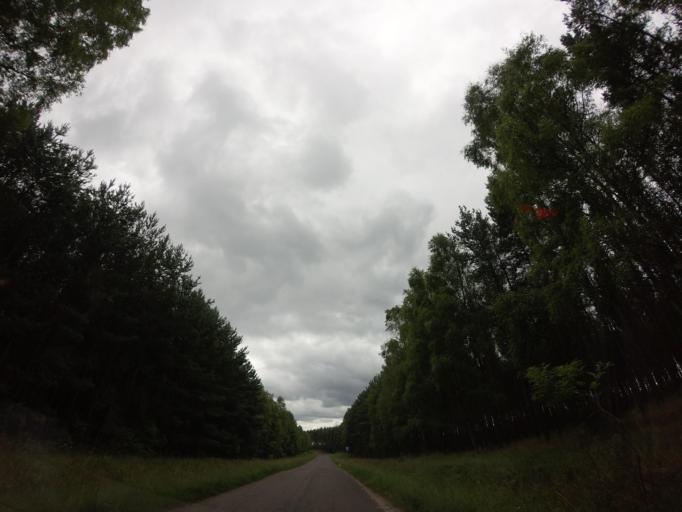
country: PL
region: West Pomeranian Voivodeship
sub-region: Powiat stargardzki
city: Insko
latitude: 53.3836
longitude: 15.5966
